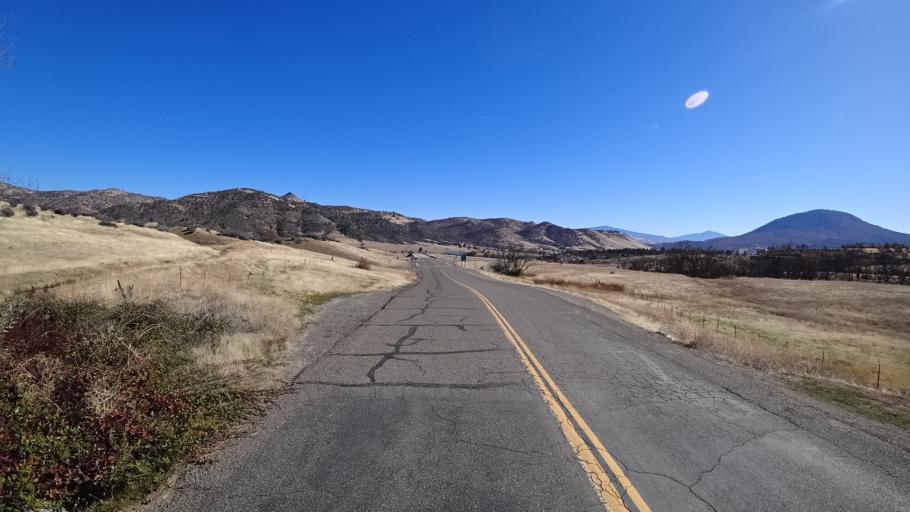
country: US
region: California
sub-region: Siskiyou County
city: Yreka
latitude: 41.9194
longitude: -122.5779
